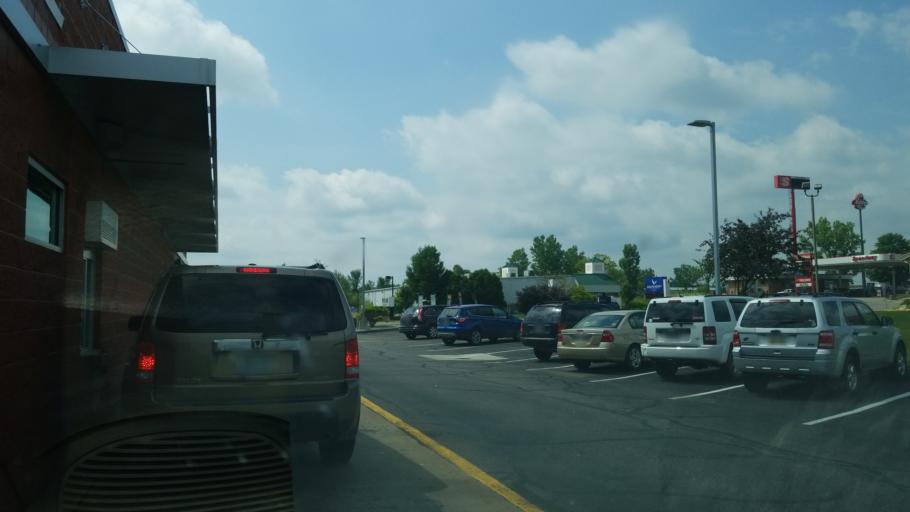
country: US
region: Michigan
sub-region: Kent County
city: Cedar Springs
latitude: 43.2205
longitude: -85.5678
